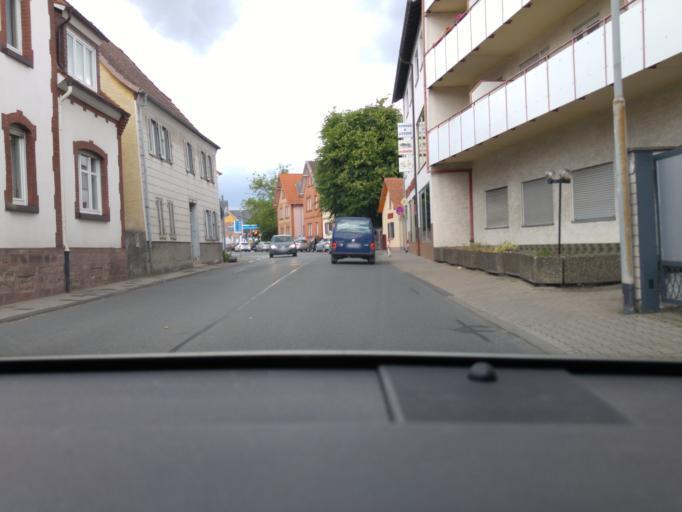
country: DE
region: Hesse
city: Langen
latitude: 49.9904
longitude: 8.6805
